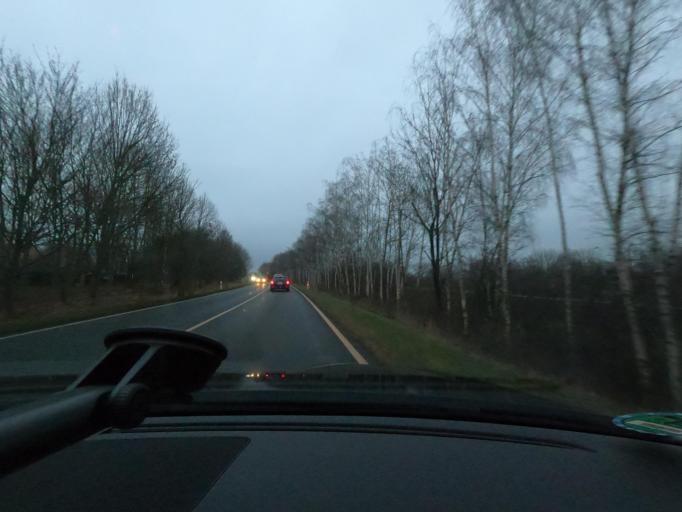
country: DE
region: Thuringia
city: Dachwig
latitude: 51.0750
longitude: 10.8586
